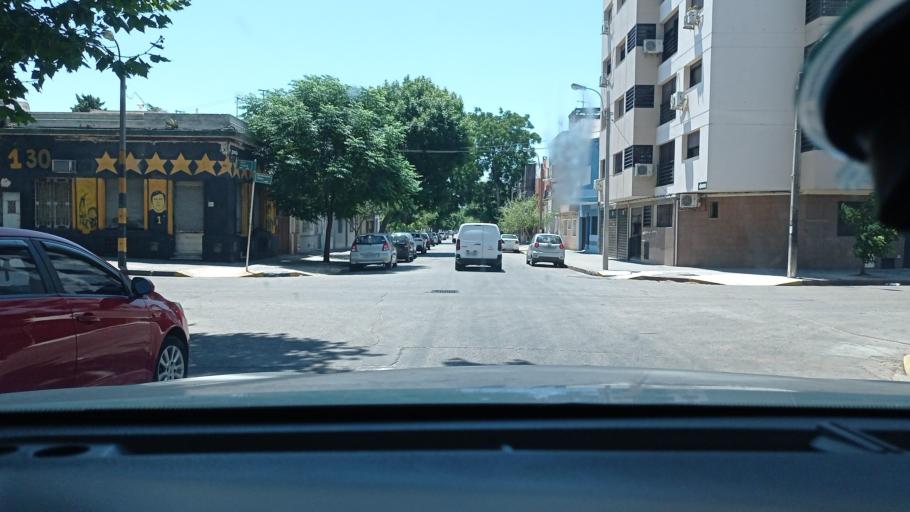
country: UY
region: Montevideo
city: Montevideo
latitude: -34.8901
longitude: -56.1668
